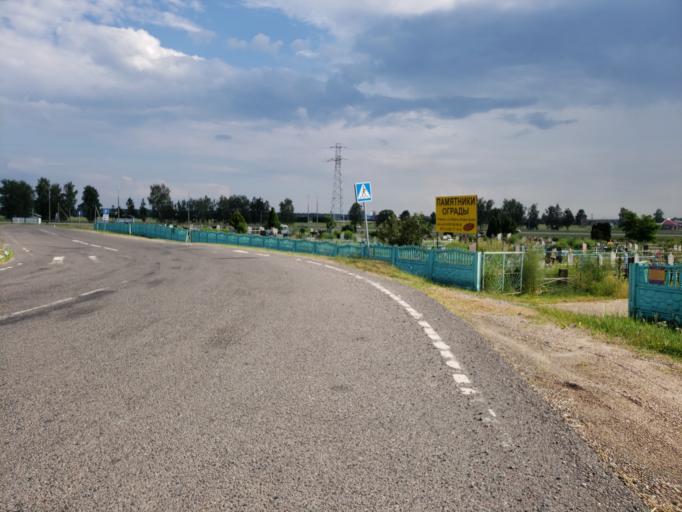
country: BY
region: Minsk
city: Chervyen'
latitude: 53.7259
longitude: 28.3919
